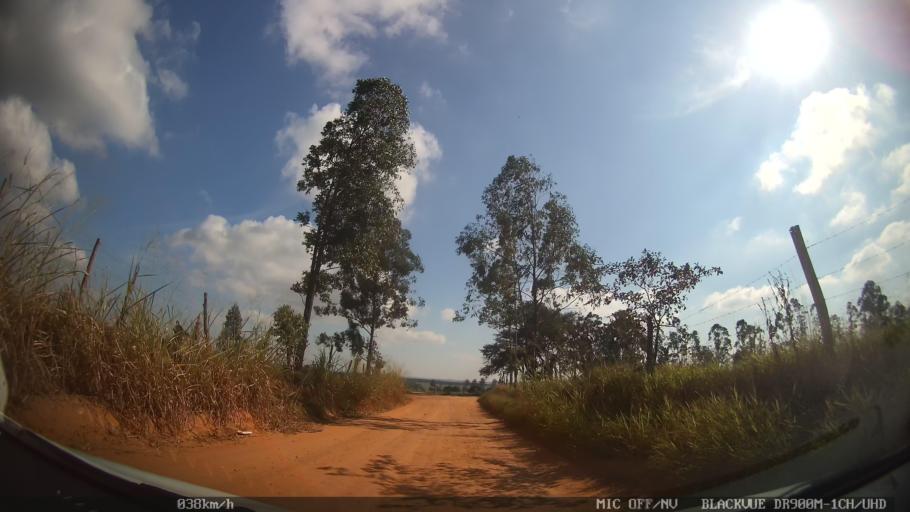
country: BR
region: Sao Paulo
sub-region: Indaiatuba
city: Indaiatuba
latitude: -22.9943
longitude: -47.2108
